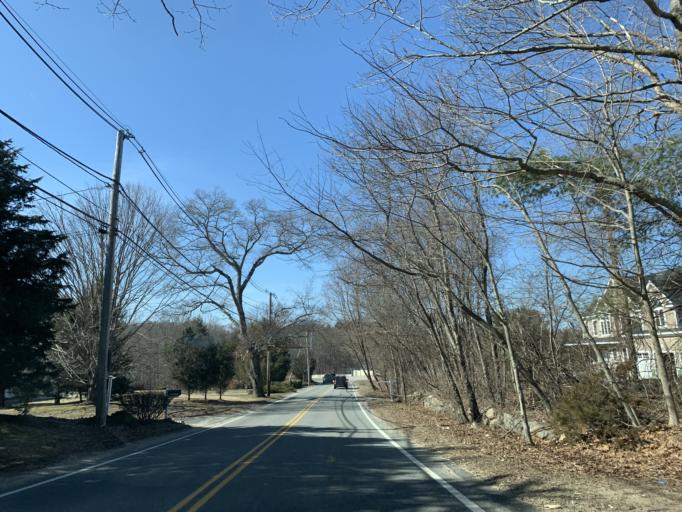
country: US
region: Massachusetts
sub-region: Norfolk County
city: Sharon
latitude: 42.1478
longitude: -71.1859
